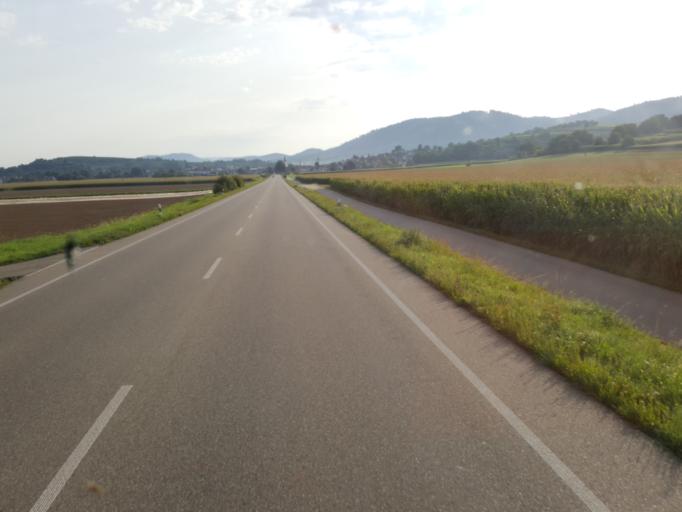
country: DE
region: Baden-Wuerttemberg
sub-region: Freiburg Region
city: Friesenheim
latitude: 48.3642
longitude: 7.8601
